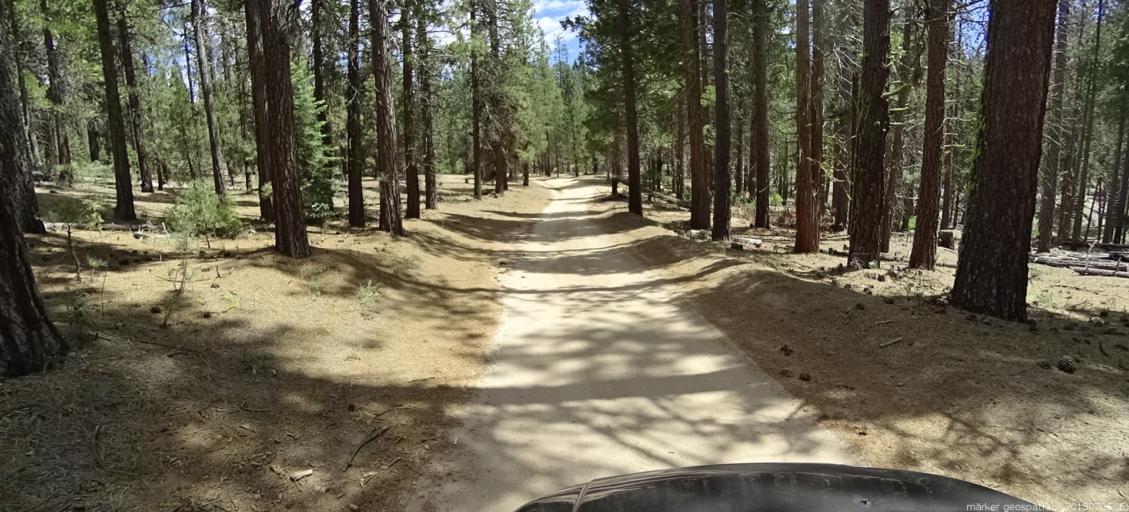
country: US
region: California
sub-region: Madera County
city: Oakhurst
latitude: 37.4158
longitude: -119.3824
